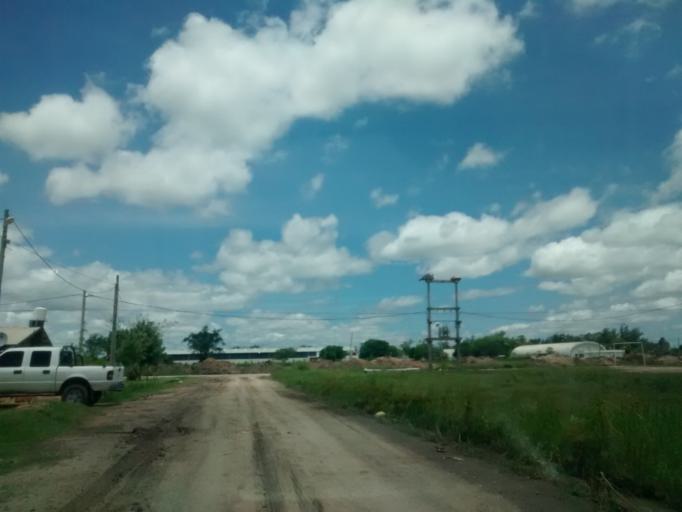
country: AR
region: Chaco
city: Fontana
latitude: -27.4041
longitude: -58.9857
